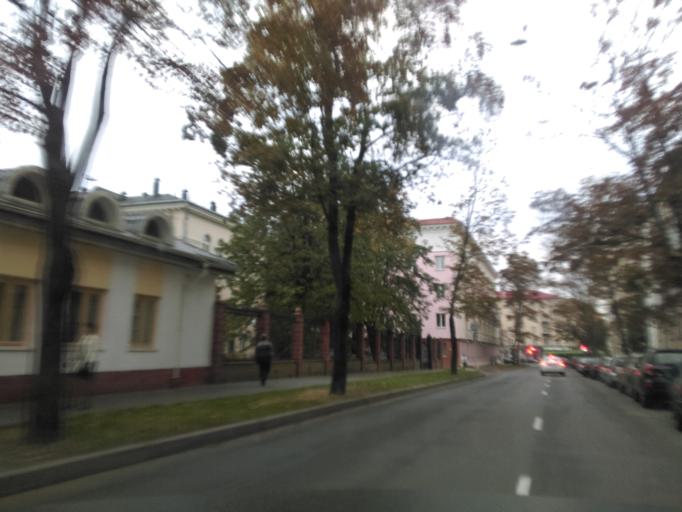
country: BY
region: Minsk
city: Minsk
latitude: 53.9103
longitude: 27.5821
